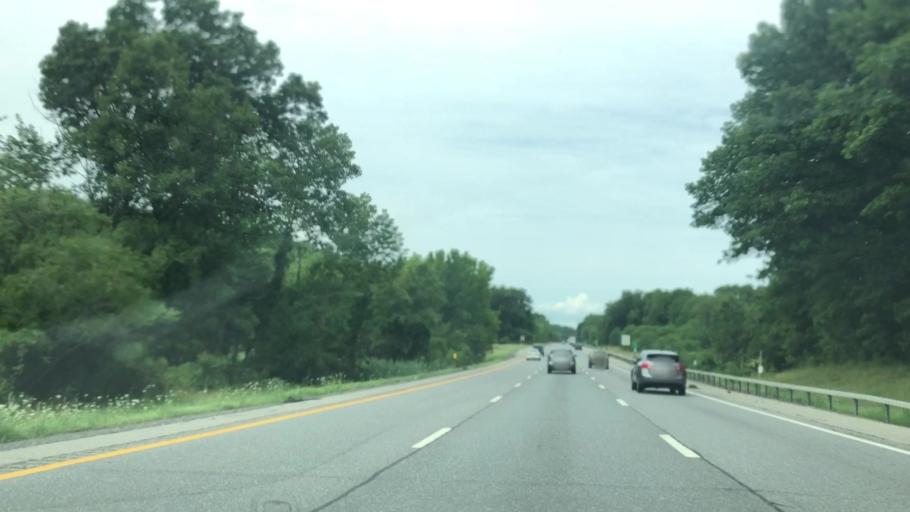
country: US
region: New York
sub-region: Saratoga County
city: Country Knolls
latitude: 42.9094
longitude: -73.7912
